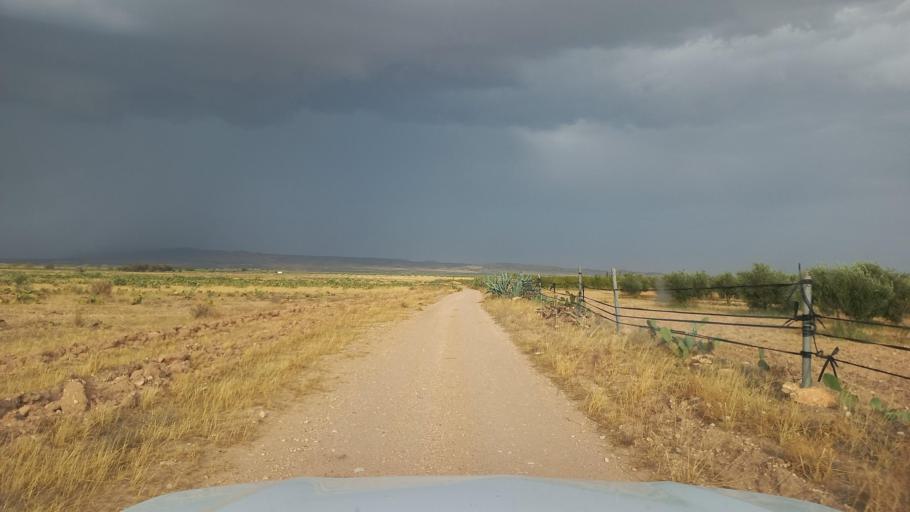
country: TN
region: Al Qasrayn
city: Kasserine
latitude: 35.2871
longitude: 9.0397
